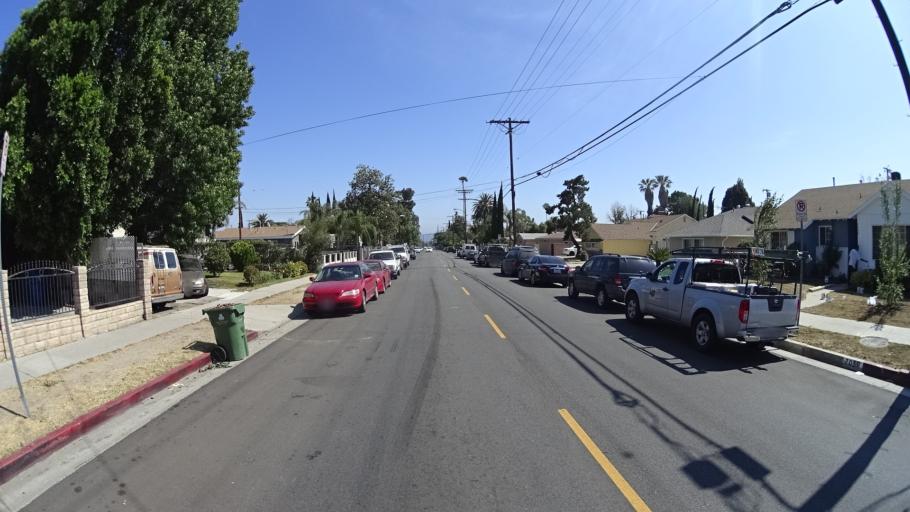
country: US
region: California
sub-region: Los Angeles County
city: Van Nuys
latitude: 34.1992
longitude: -118.4181
